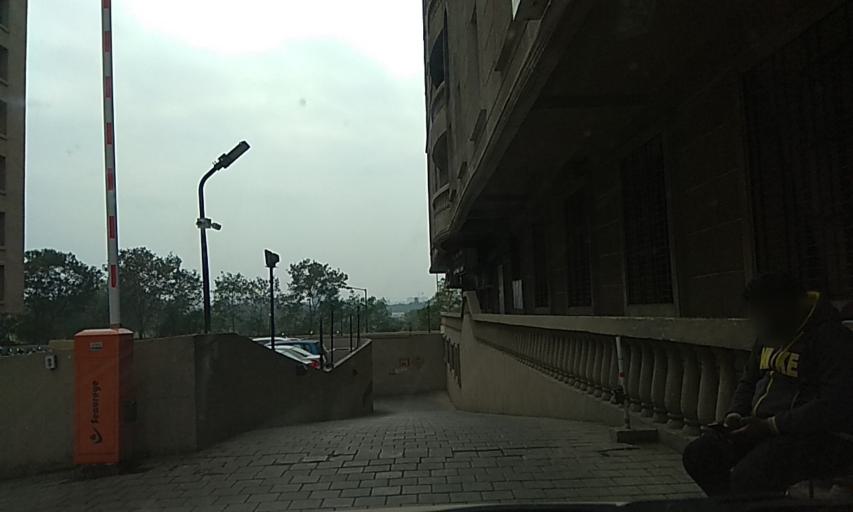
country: IN
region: Maharashtra
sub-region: Pune Division
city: Lohogaon
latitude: 18.5448
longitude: 73.9105
